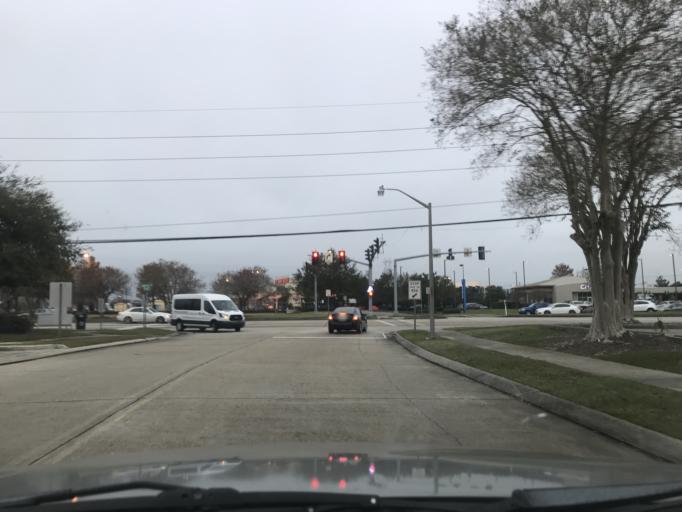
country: US
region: Louisiana
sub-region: Jefferson Parish
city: Woodmere
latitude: 29.8739
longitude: -90.0906
